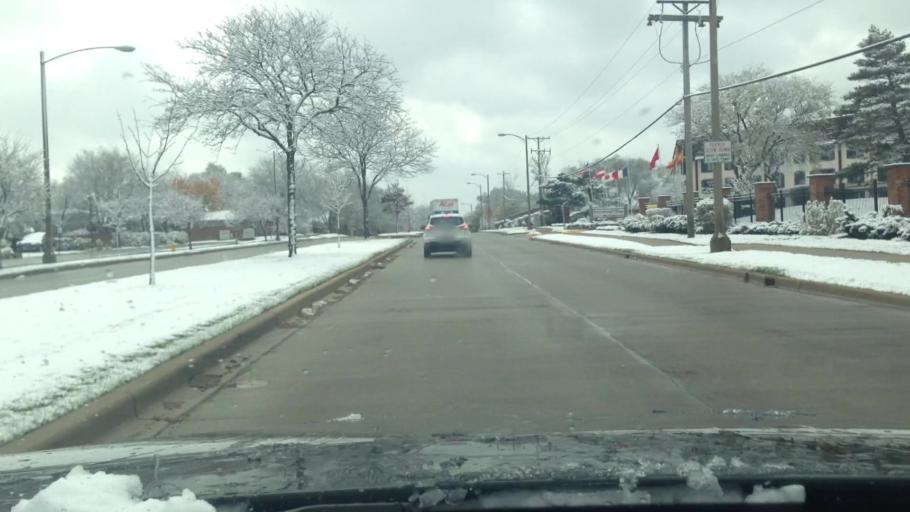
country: US
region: Illinois
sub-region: DuPage County
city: Lombard
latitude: 41.8574
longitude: -88.0270
